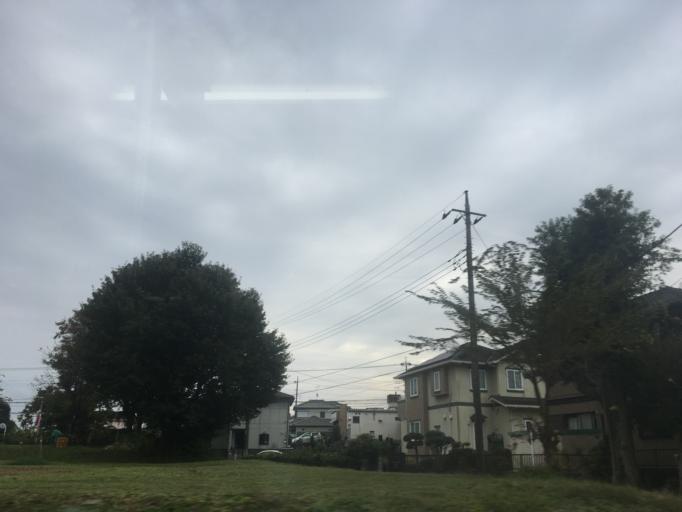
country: JP
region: Saitama
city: Sakado
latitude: 35.9066
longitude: 139.4009
